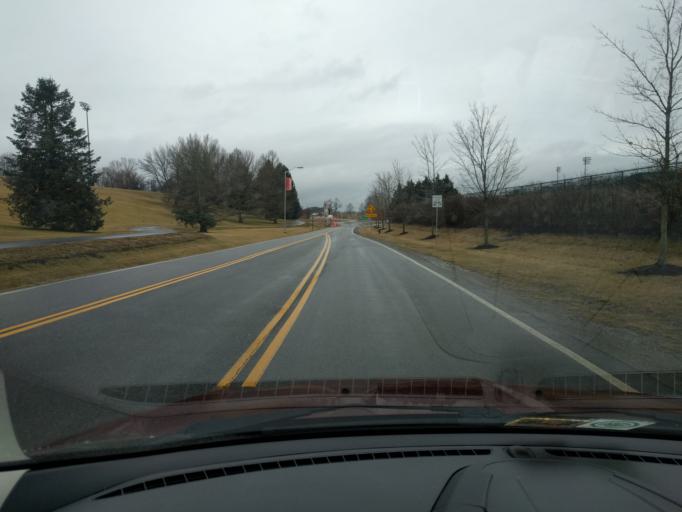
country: US
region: Virginia
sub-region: Montgomery County
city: Blacksburg
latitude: 37.2171
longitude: -80.4205
